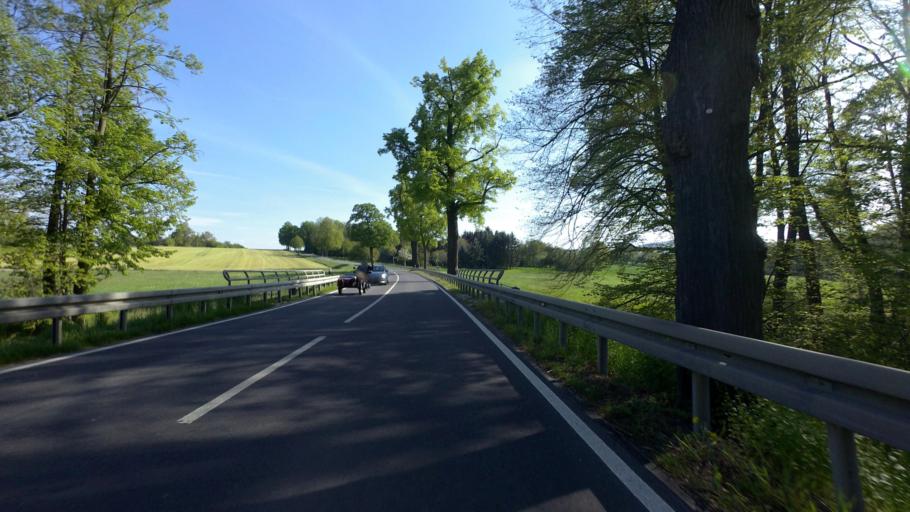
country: DE
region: Saxony
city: Elstra
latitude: 51.2162
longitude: 14.1334
